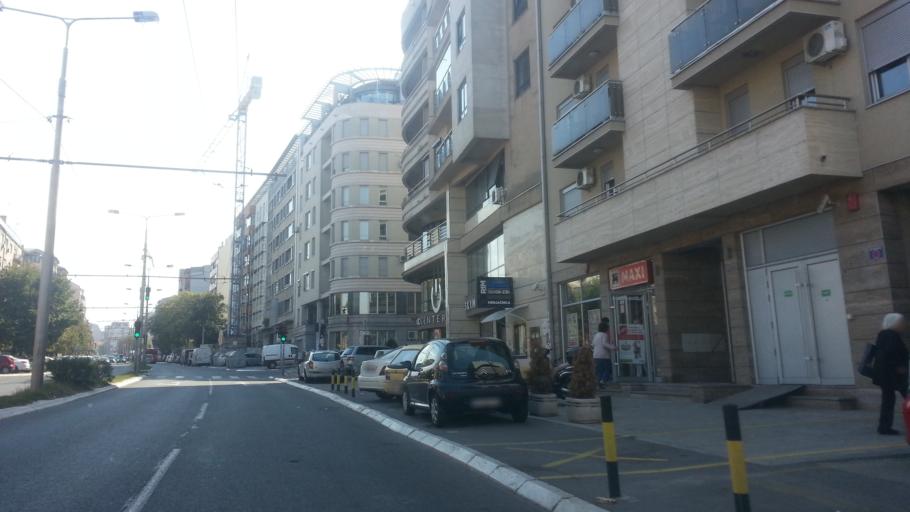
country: RS
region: Central Serbia
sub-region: Belgrade
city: Vracar
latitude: 44.8052
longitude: 20.4847
